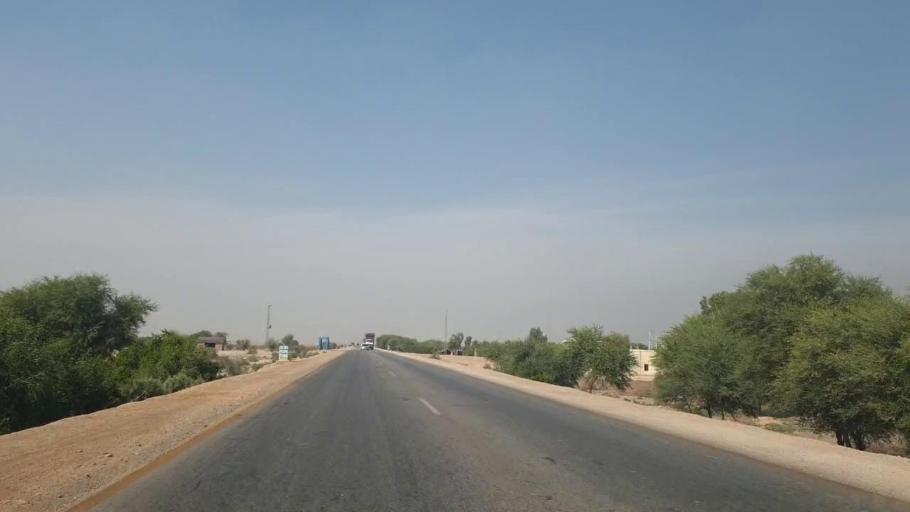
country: PK
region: Sindh
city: Hala
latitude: 25.8754
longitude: 68.2517
